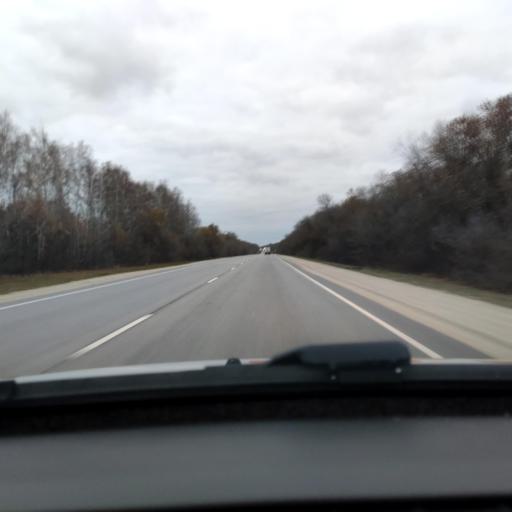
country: RU
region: Lipetsk
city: Borinskoye
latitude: 52.3789
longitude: 39.2171
